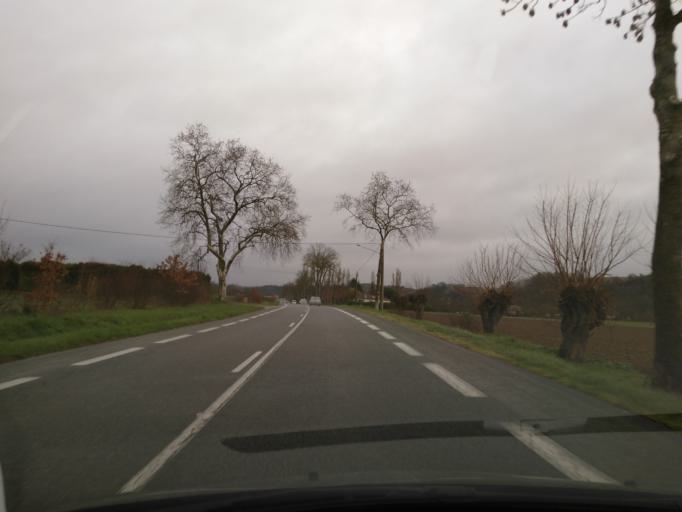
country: FR
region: Midi-Pyrenees
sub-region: Departement de la Haute-Garonne
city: Carbonne
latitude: 43.2781
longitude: 1.2092
